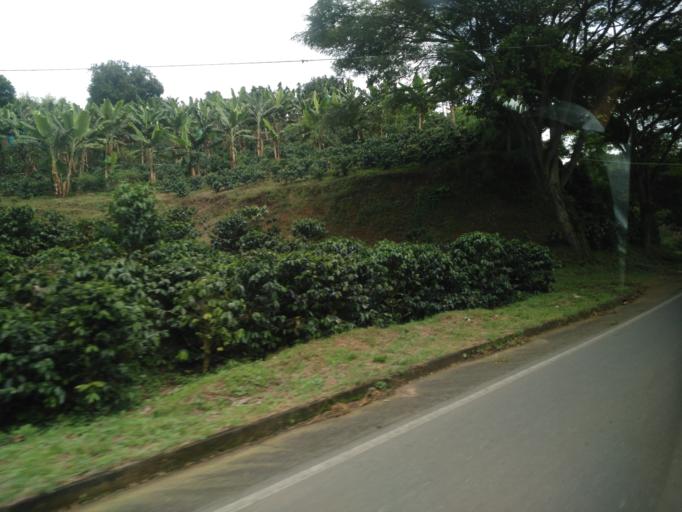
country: CO
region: Valle del Cauca
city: Caicedonia
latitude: 4.3137
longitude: -75.8785
